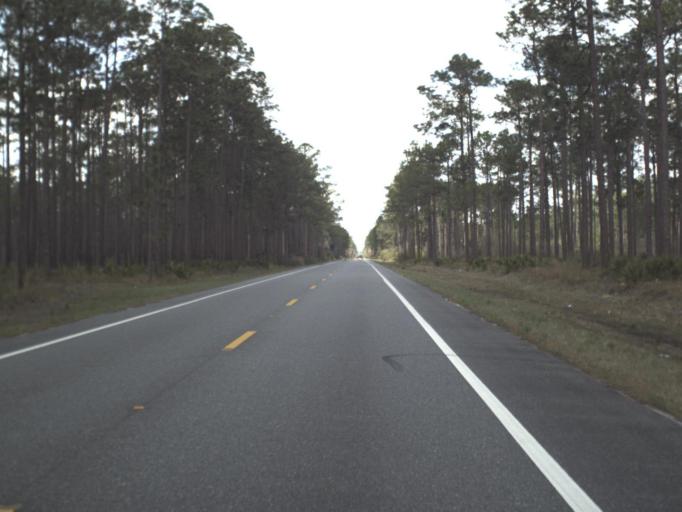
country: US
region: Florida
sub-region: Franklin County
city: Apalachicola
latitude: 29.9789
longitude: -84.9753
